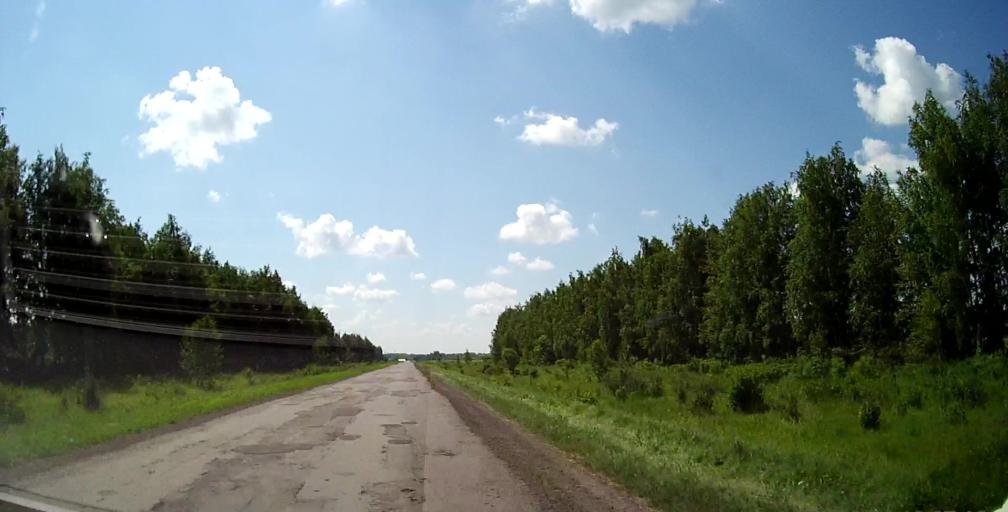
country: RU
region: Lipetsk
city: Chaplygin
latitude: 53.3612
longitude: 39.9205
